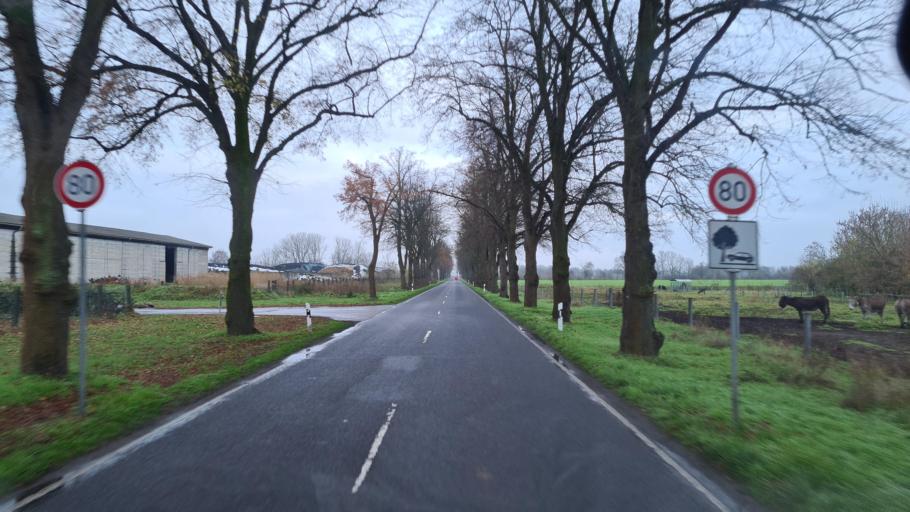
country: DE
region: Brandenburg
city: Nauen
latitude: 52.6605
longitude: 12.8222
